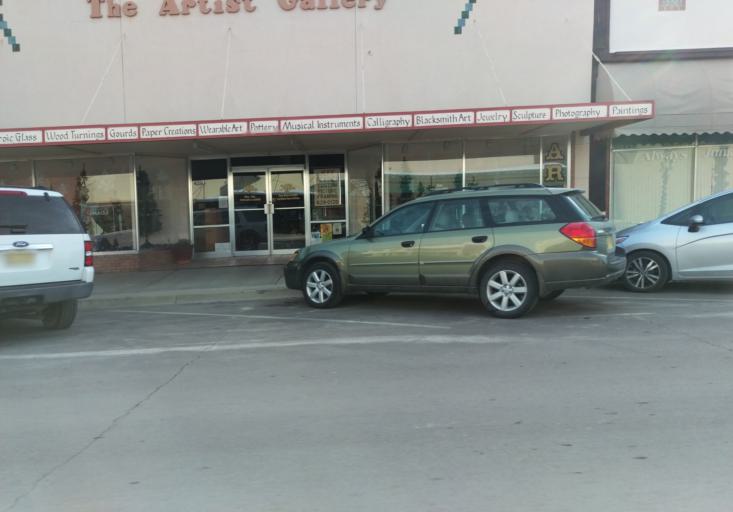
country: US
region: New Mexico
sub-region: Eddy County
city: Carlsbad
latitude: 32.4196
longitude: -104.2277
